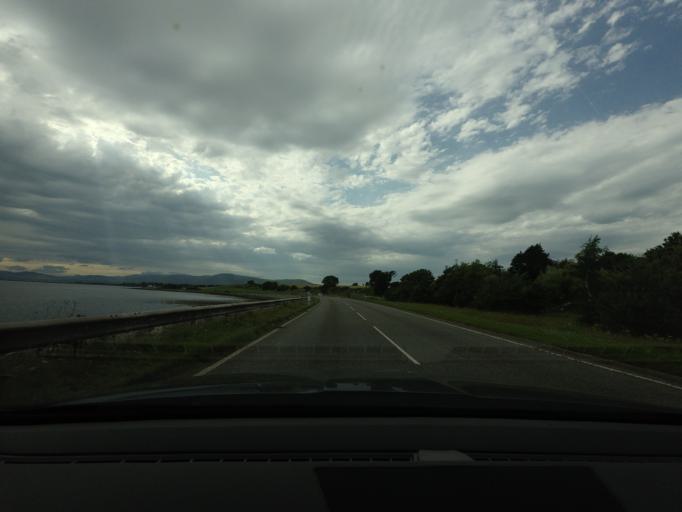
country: GB
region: Scotland
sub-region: Highland
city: Invergordon
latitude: 57.6923
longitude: -4.2005
